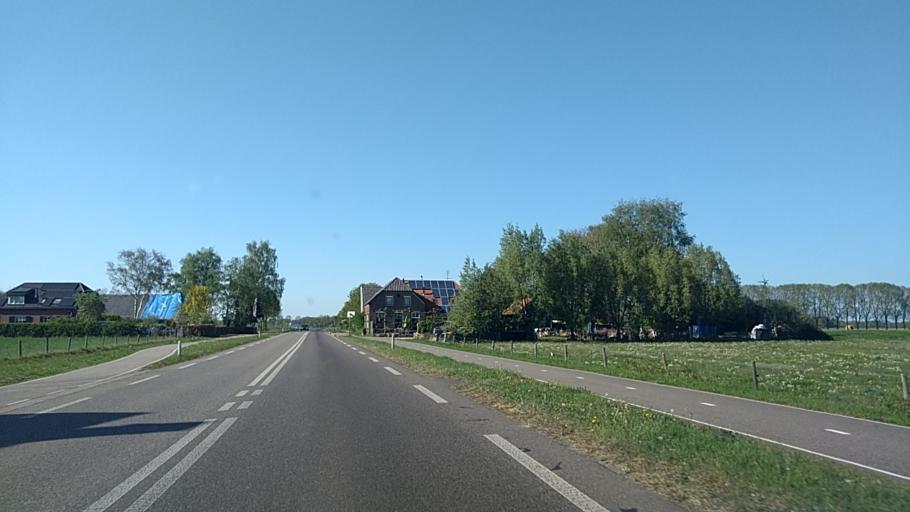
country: NL
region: Gelderland
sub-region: Gemeente Bronckhorst
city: Baak
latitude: 52.0806
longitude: 6.2251
